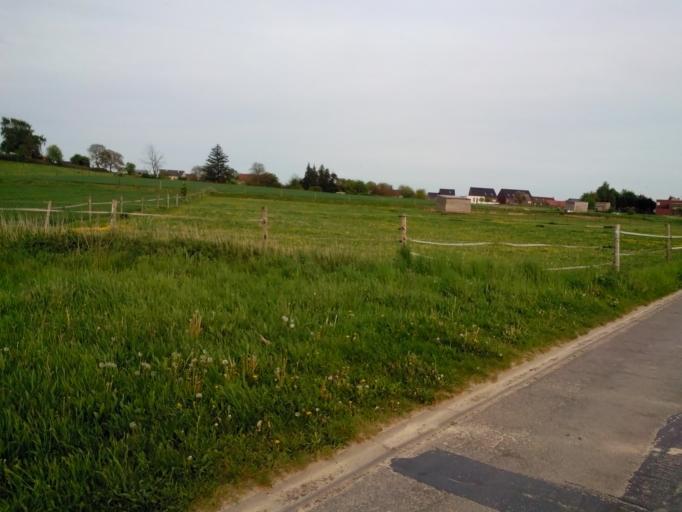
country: BE
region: Flanders
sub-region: Provincie Vlaams-Brabant
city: Bierbeek
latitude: 50.8391
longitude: 4.7255
